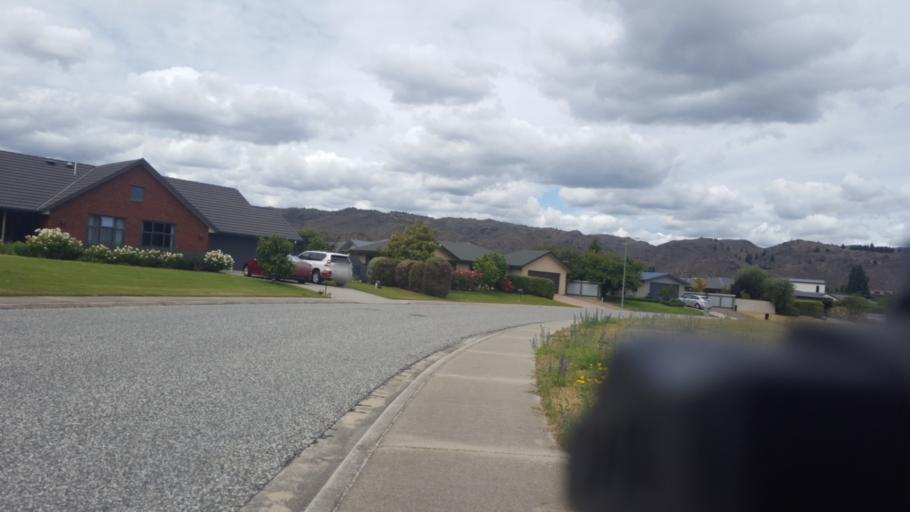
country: NZ
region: Otago
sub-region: Queenstown-Lakes District
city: Wanaka
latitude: -45.2538
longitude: 169.3846
